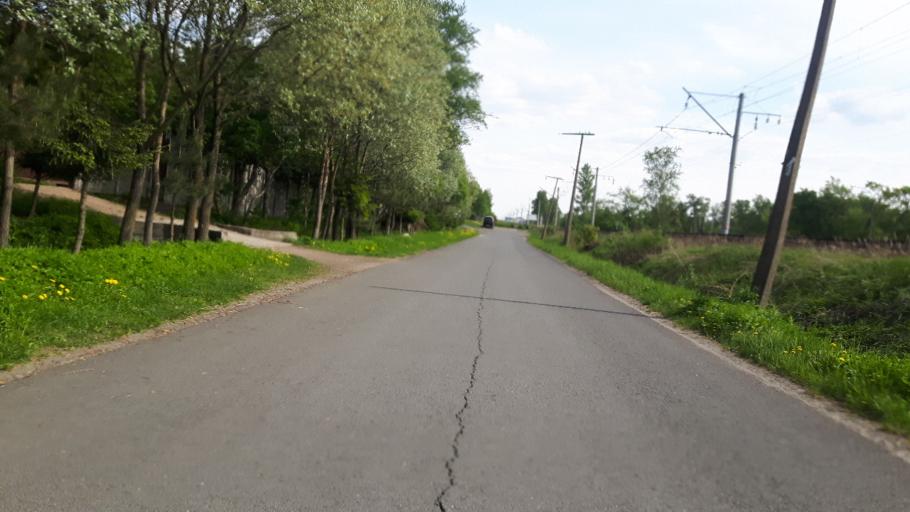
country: RU
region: Leningrad
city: Gorskaya
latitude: 60.0345
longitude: 29.9825
